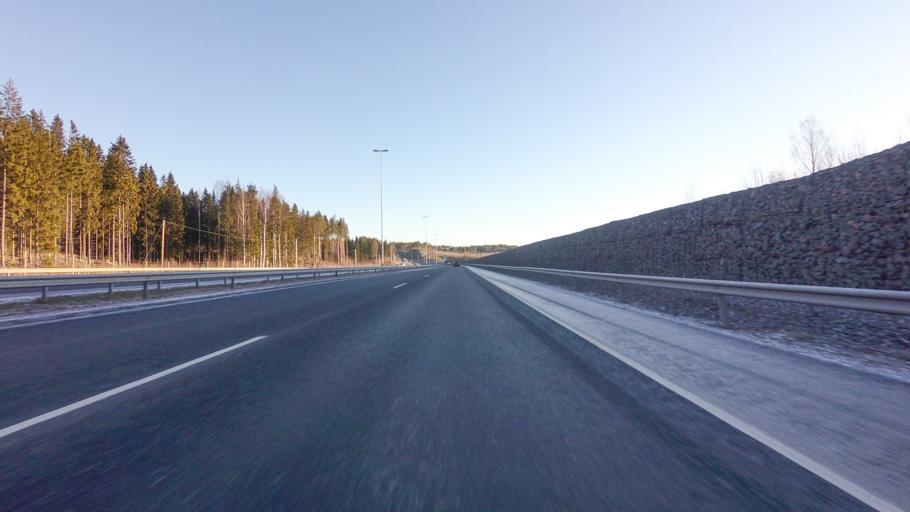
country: FI
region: Uusimaa
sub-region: Helsinki
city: Lohja
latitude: 60.2860
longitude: 24.0885
